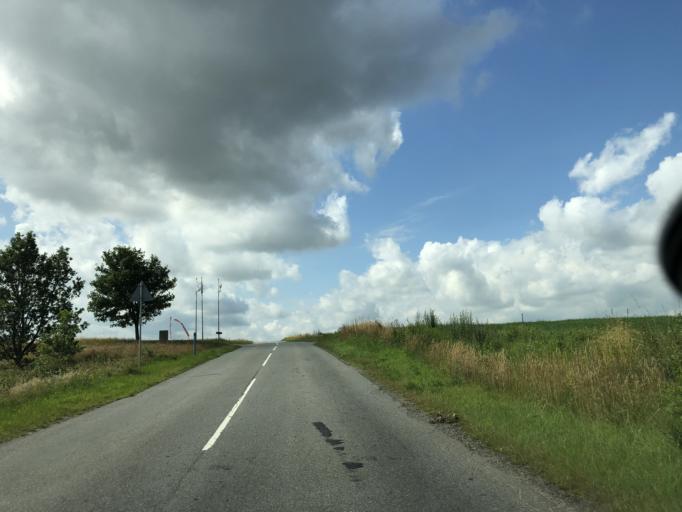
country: DK
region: Central Jutland
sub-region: Ikast-Brande Kommune
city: Brande
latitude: 55.9593
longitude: 9.1477
